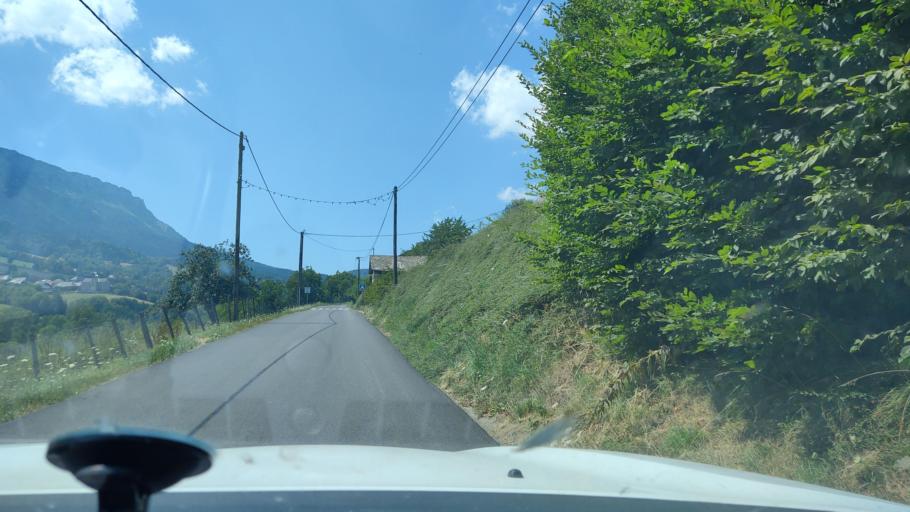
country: FR
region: Rhone-Alpes
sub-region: Departement de la Haute-Savoie
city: Cusy
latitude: 45.6886
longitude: 6.0650
